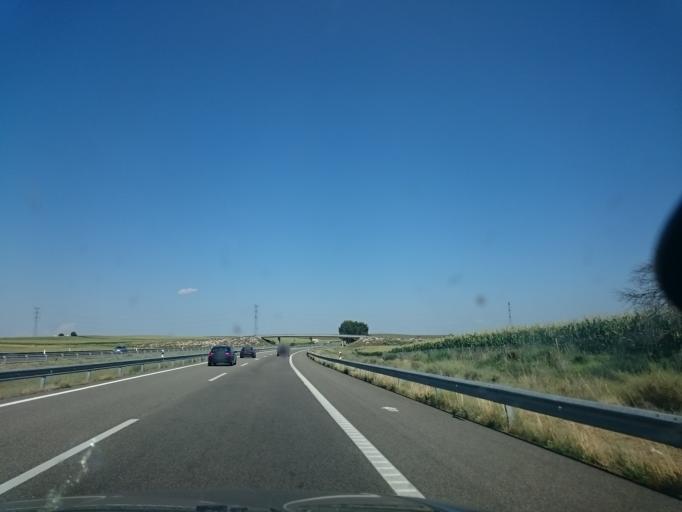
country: ES
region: Aragon
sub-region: Provincia de Huesca
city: Penalba
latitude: 41.5180
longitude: -0.0907
